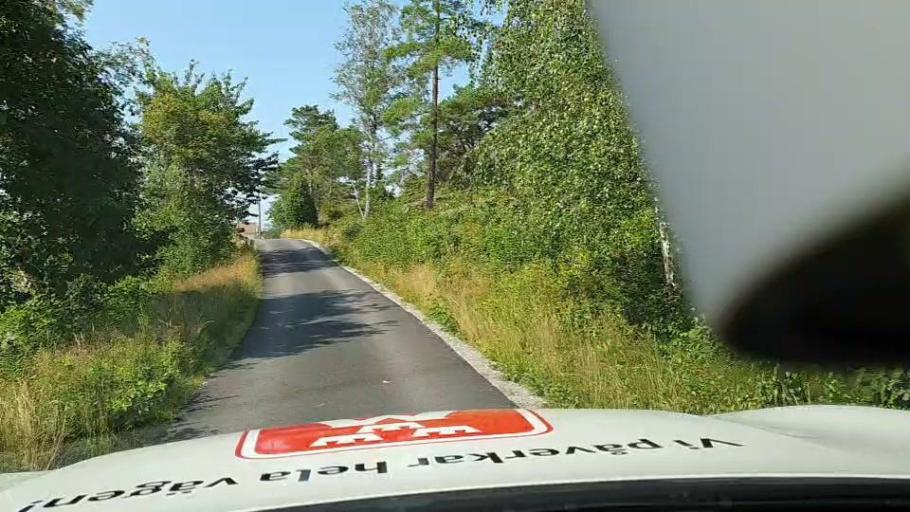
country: SE
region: Vaestra Goetaland
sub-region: Tjorns Kommun
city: Myggenas
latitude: 58.1118
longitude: 11.6485
